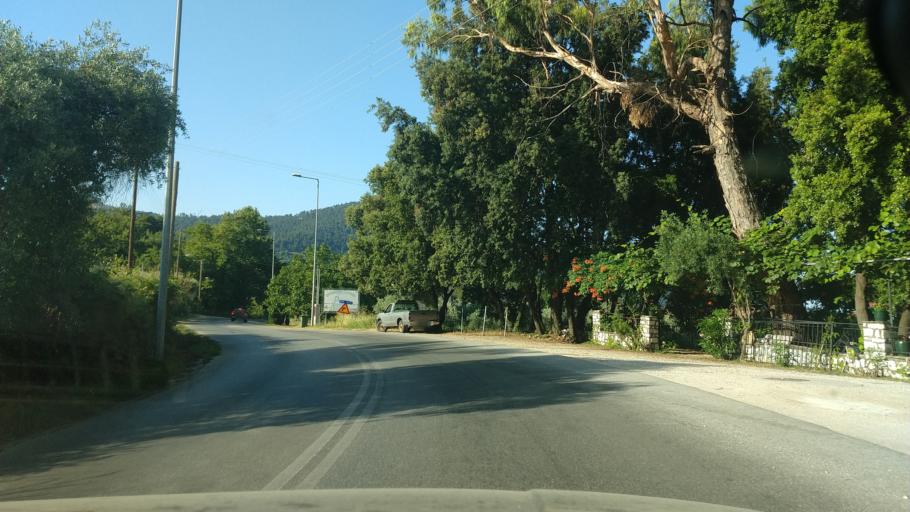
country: GR
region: East Macedonia and Thrace
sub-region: Nomos Kavalas
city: Potamia
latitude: 40.7145
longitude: 24.7379
